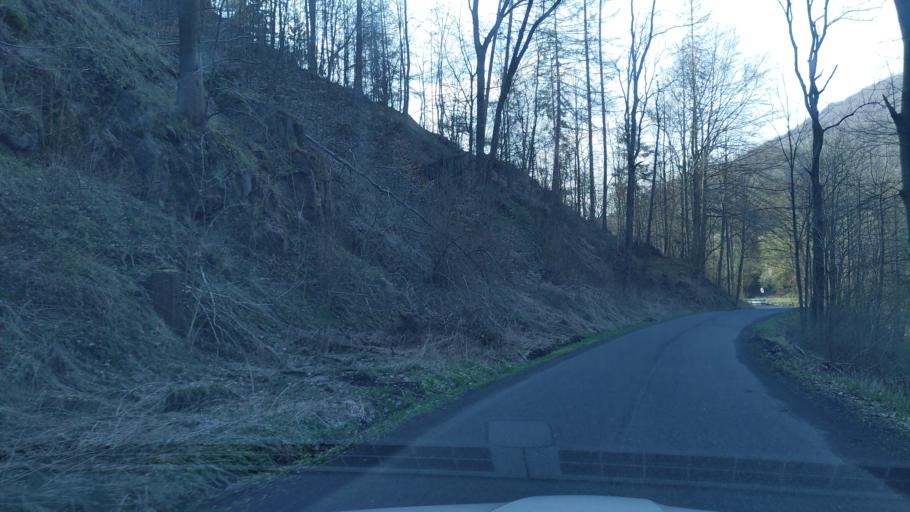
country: CZ
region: Ustecky
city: Povrly
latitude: 50.7029
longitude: 14.2319
